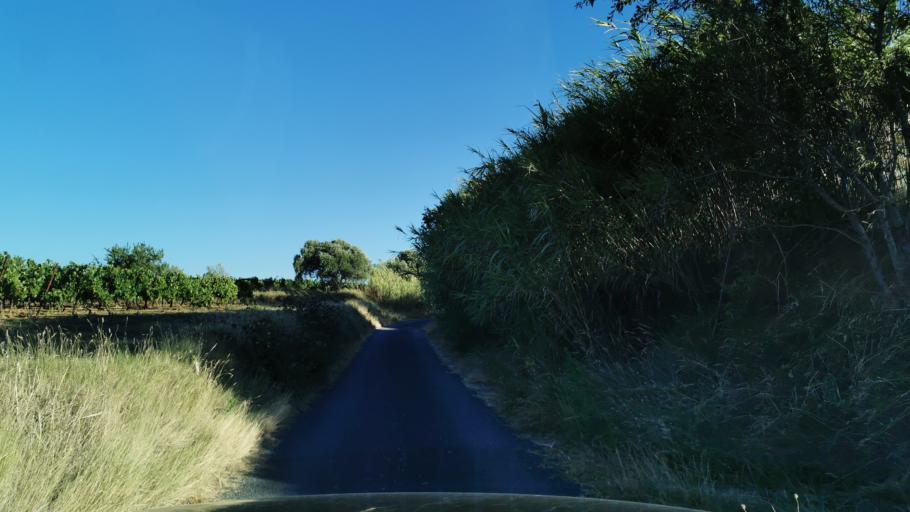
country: FR
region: Languedoc-Roussillon
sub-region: Departement de l'Aude
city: Ouveillan
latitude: 43.2762
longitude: 2.9769
